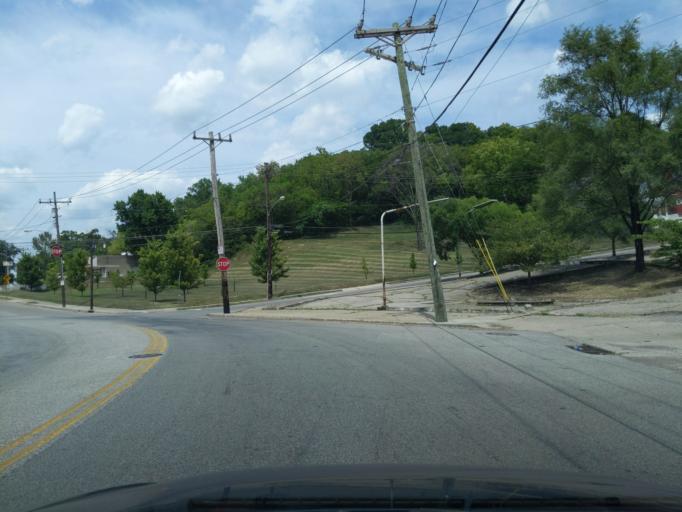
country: US
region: Kentucky
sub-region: Kenton County
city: Ludlow
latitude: 39.1317
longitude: -84.5302
